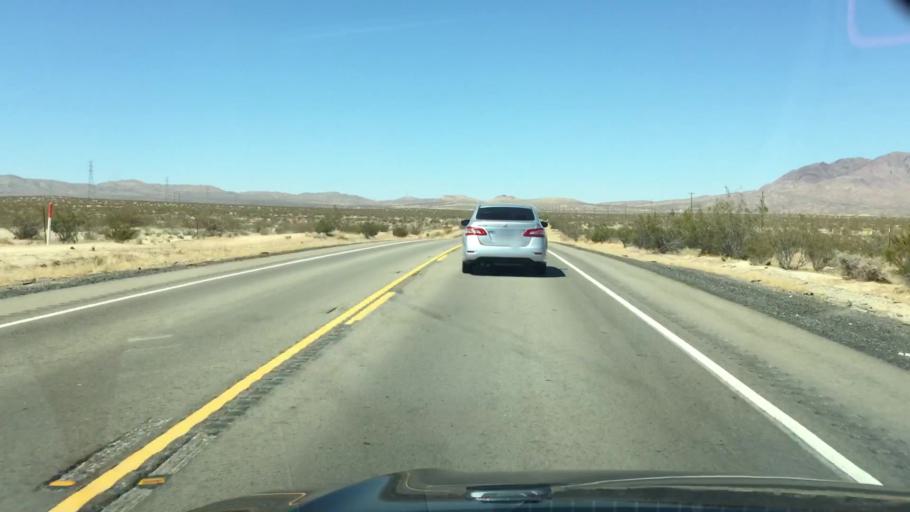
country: US
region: California
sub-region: Kern County
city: Boron
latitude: 35.2612
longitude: -117.6130
